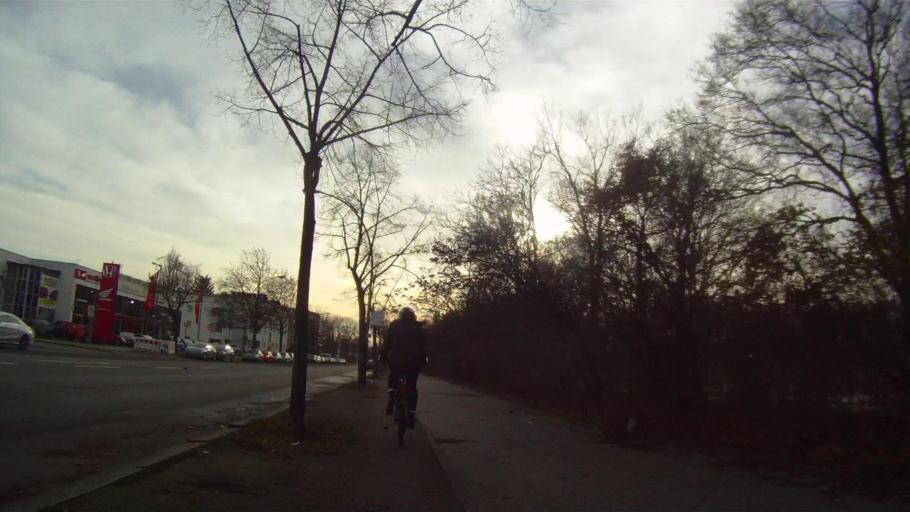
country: DE
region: Berlin
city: Britz
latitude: 52.4545
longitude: 13.4508
